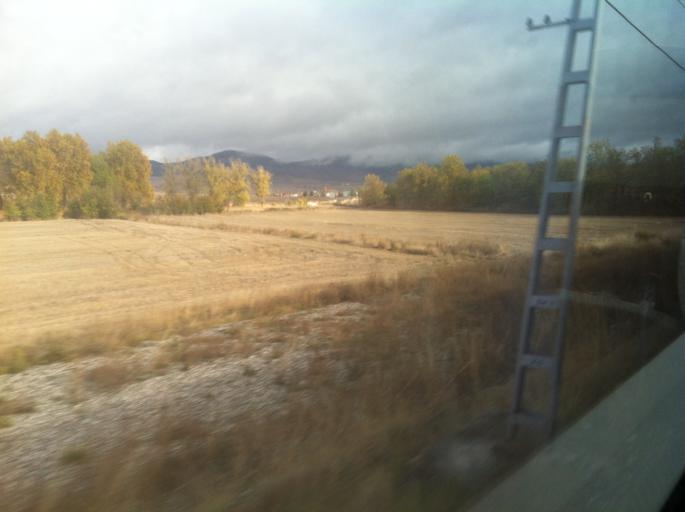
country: ES
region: Castille and Leon
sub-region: Provincia de Burgos
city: Fuentebureba
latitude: 42.6241
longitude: -3.2422
